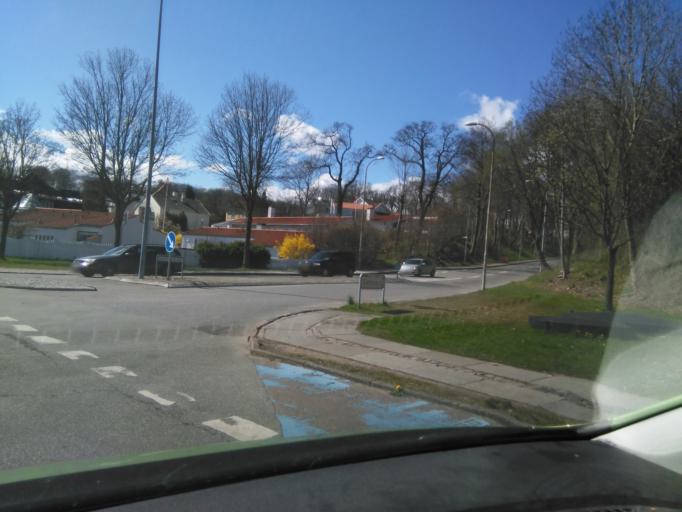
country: DK
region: Central Jutland
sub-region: Arhus Kommune
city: Arhus
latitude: 56.1840
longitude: 10.2360
